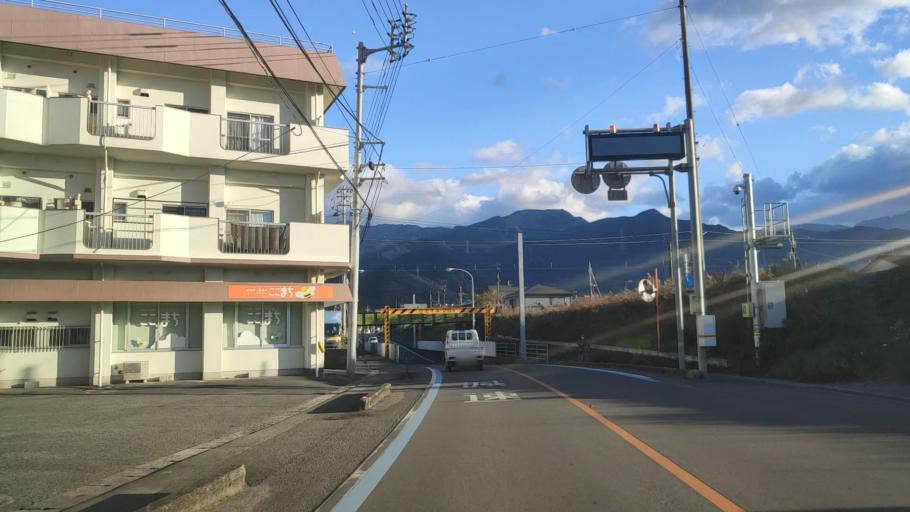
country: JP
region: Ehime
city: Saijo
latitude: 33.9097
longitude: 133.1818
